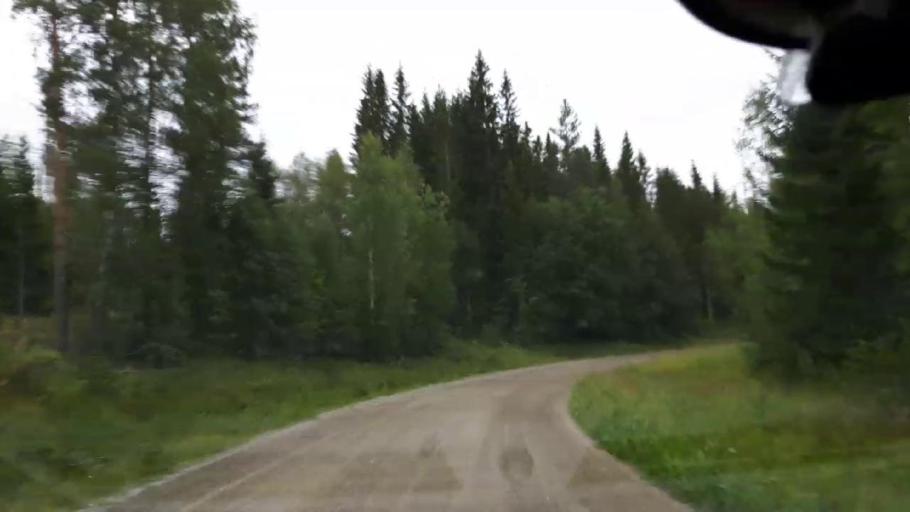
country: SE
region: Jaemtland
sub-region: Braecke Kommun
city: Braecke
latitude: 63.0044
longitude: 15.3829
